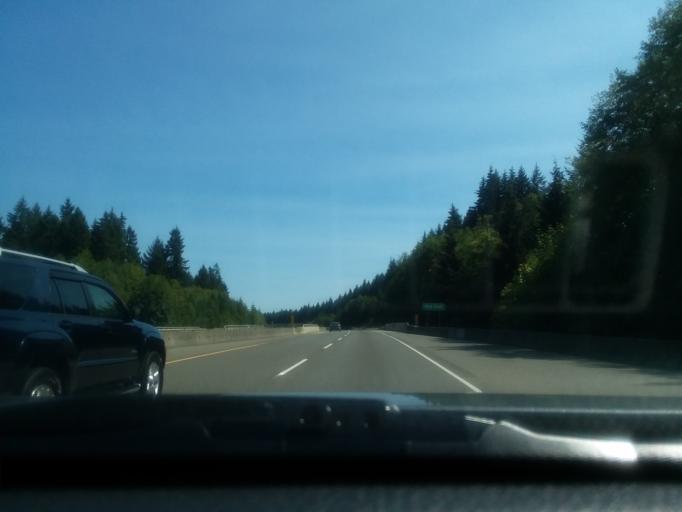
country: CA
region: British Columbia
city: Port Alberni
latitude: 49.4243
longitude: -124.7281
